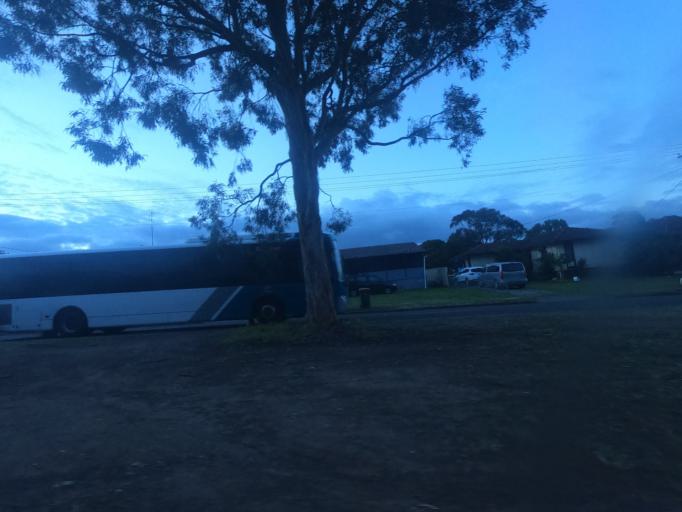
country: AU
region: New South Wales
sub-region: Wollongong
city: Koonawarra
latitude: -34.5029
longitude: 150.8046
